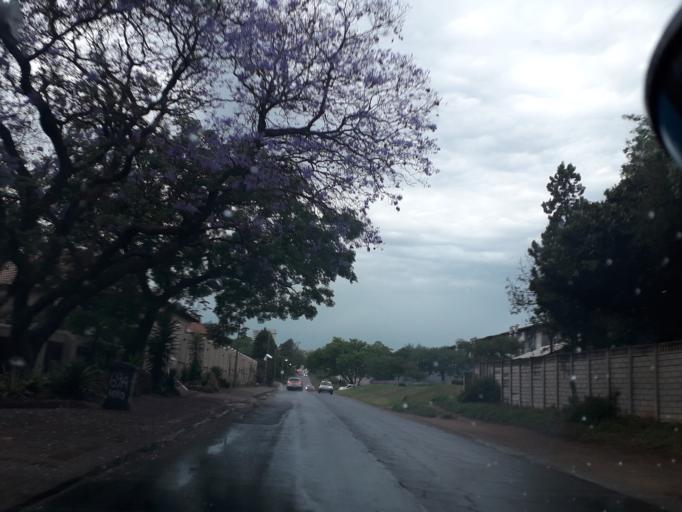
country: ZA
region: Gauteng
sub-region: City of Johannesburg Metropolitan Municipality
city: Johannesburg
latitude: -26.0845
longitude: 27.9911
